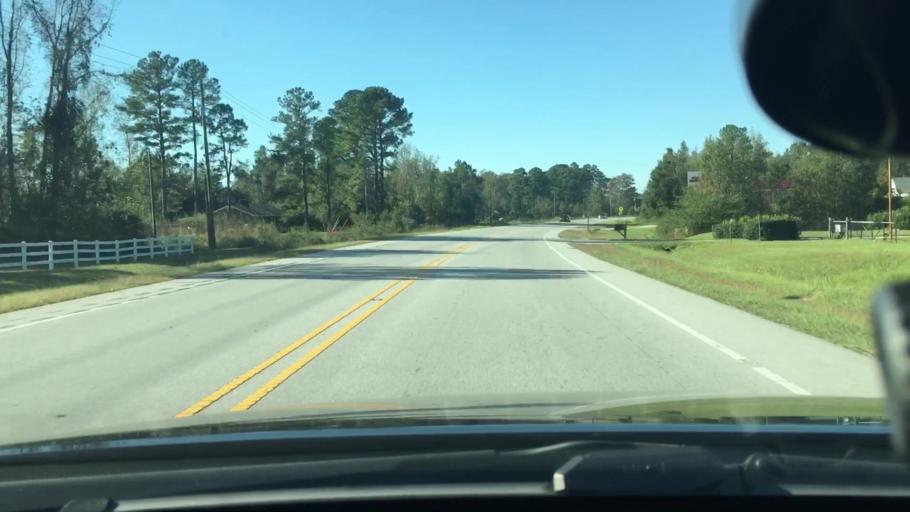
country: US
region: North Carolina
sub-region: Craven County
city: Trent Woods
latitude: 35.1596
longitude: -77.1166
